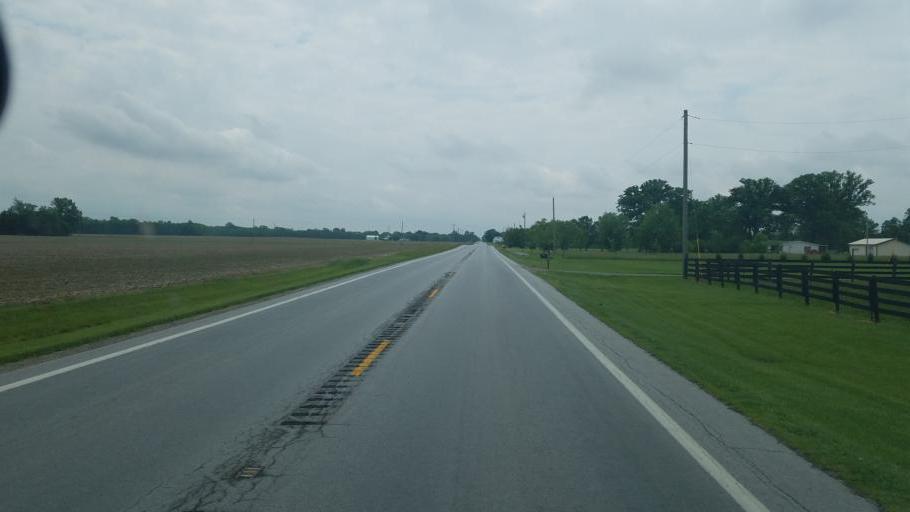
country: US
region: Ohio
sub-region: Union County
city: Richwood
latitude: 40.3589
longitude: -83.2963
